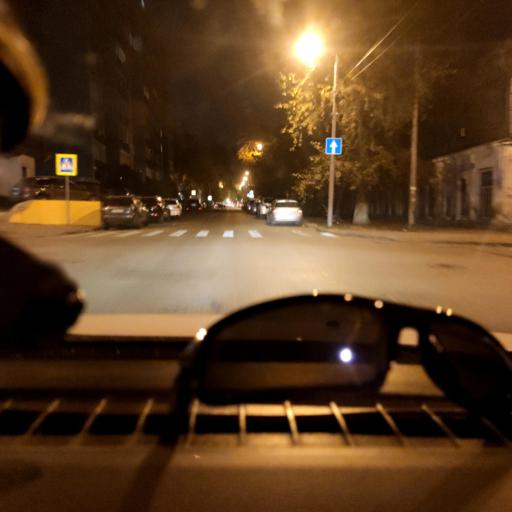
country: RU
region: Samara
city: Samara
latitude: 53.2027
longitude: 50.1212
